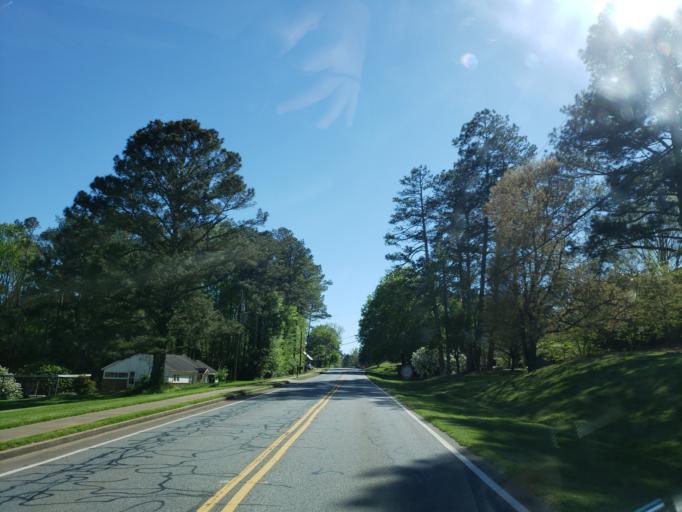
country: US
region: Georgia
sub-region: Cherokee County
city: Canton
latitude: 34.3189
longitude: -84.5506
